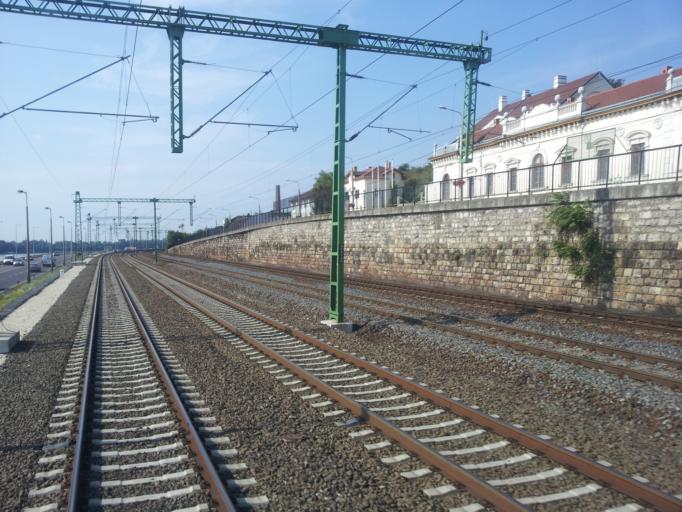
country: HU
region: Budapest
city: Budapest XXII. keruelet
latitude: 47.4195
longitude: 19.0421
